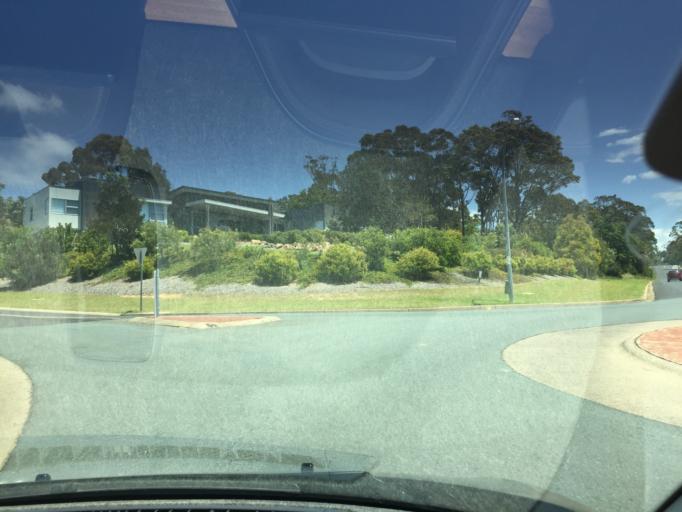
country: AU
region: New South Wales
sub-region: Bega Valley
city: Merimbula
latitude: -36.8487
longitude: 149.9275
